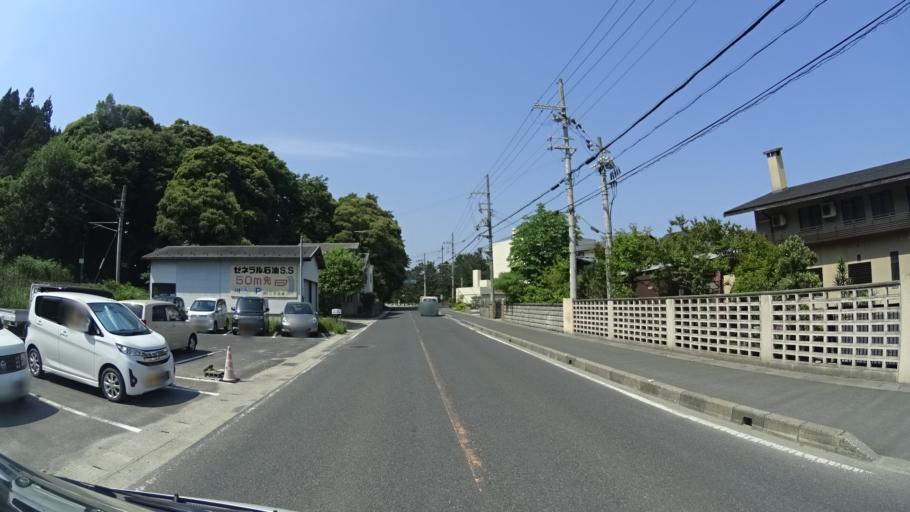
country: JP
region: Kyoto
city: Miyazu
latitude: 35.5534
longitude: 135.1868
